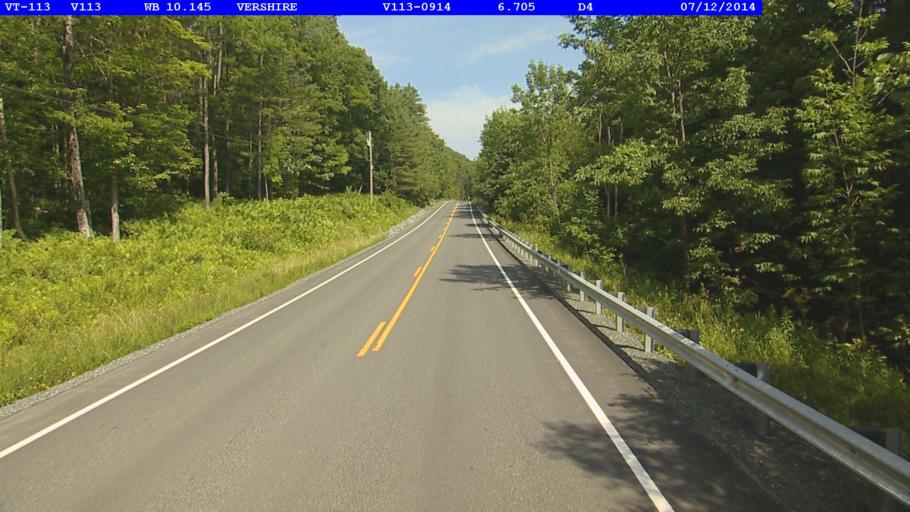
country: US
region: New Hampshire
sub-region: Grafton County
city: Orford
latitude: 43.9490
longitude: -72.2749
